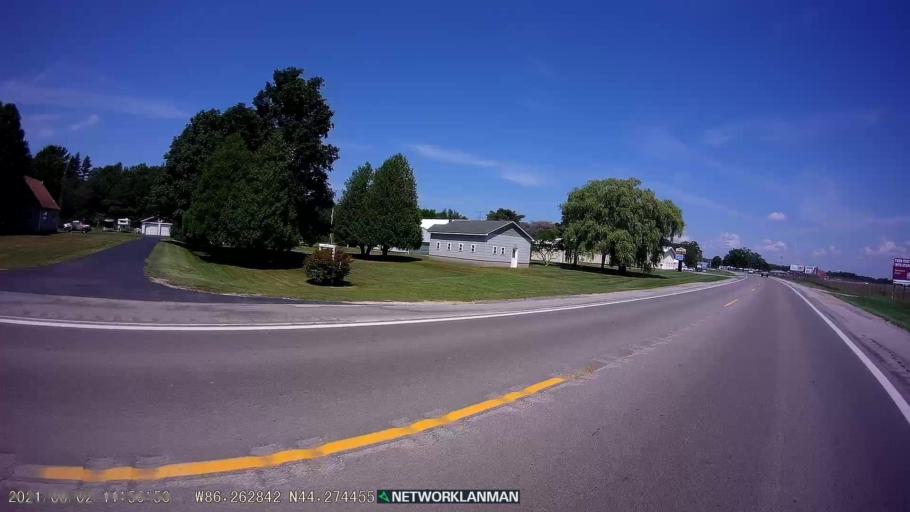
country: US
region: Michigan
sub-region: Manistee County
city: Manistee
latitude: 44.2743
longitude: -86.2624
